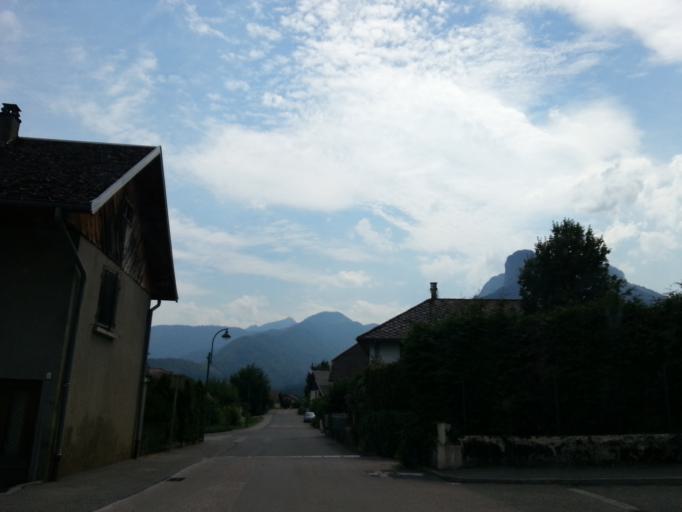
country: FR
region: Rhone-Alpes
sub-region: Departement de la Haute-Savoie
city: Doussard
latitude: 45.7848
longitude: 6.2049
